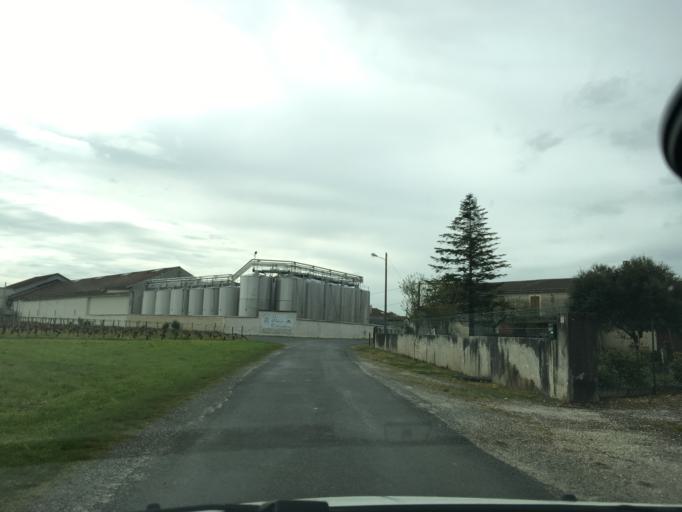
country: FR
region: Aquitaine
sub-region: Departement de la Gironde
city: Lesparre-Medoc
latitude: 45.3142
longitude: -0.8945
